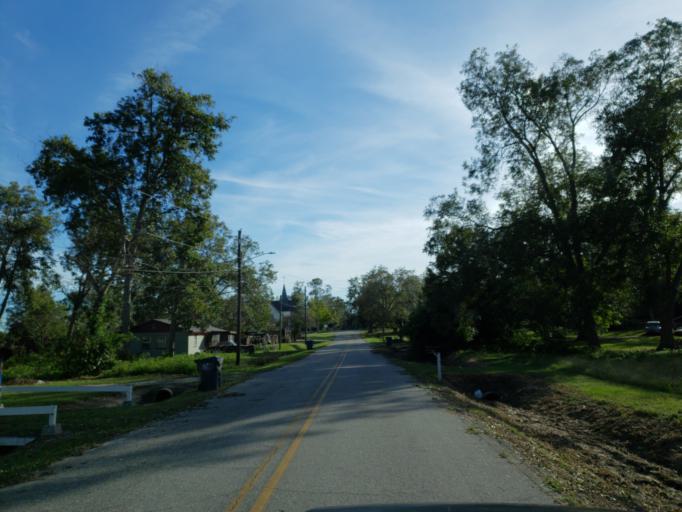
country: US
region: Georgia
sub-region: Dooly County
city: Unadilla
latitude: 32.2618
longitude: -83.7380
